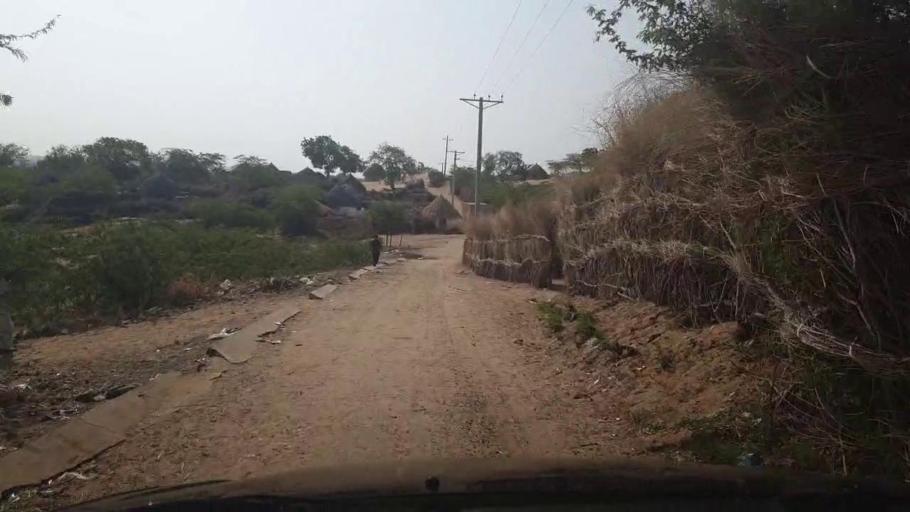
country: PK
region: Sindh
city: Islamkot
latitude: 24.9963
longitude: 70.2046
